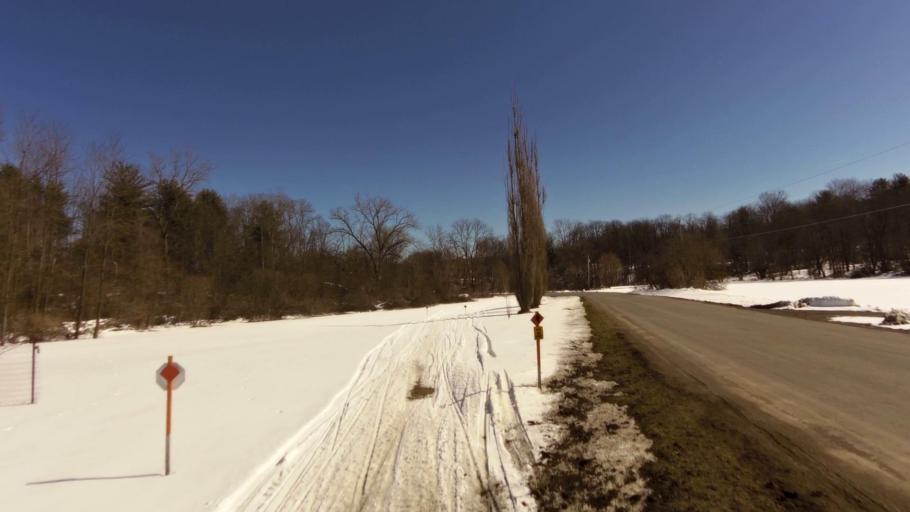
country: US
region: New York
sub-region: Allegany County
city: Houghton
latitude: 42.3622
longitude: -78.1417
